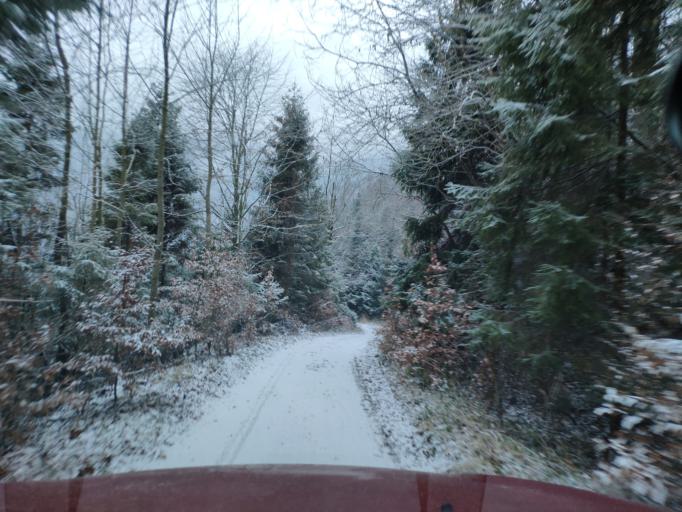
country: SK
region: Kosicky
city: Spisska Nova Ves
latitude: 48.8132
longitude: 20.5144
